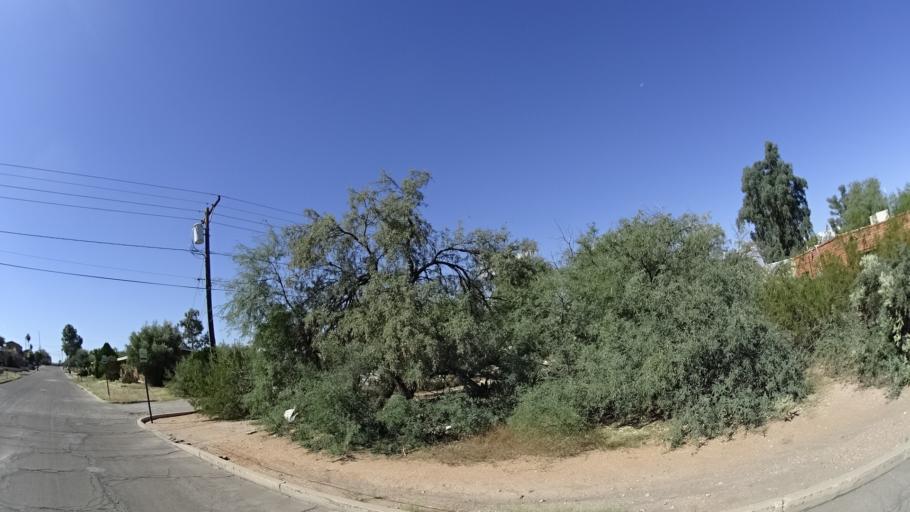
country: US
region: Arizona
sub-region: Pima County
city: Tucson
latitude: 32.2434
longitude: -110.9513
